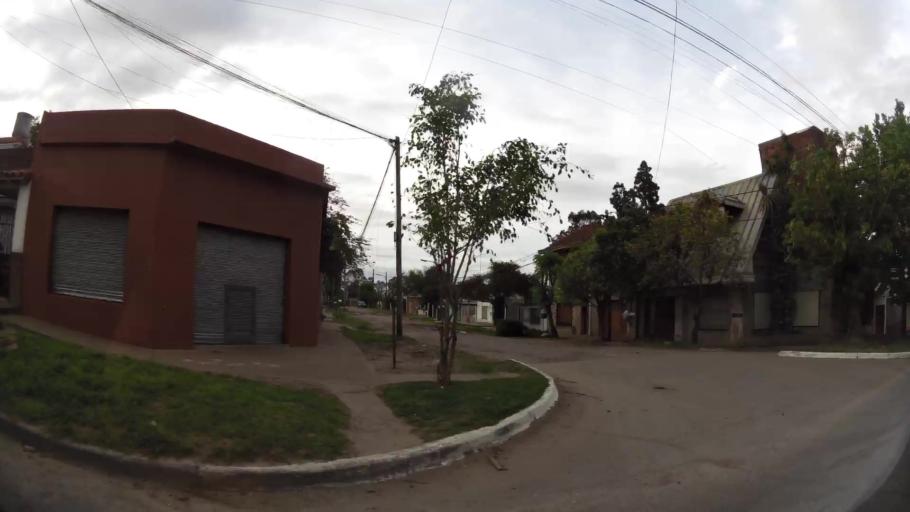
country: AR
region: Buenos Aires
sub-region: Partido de Quilmes
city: Quilmes
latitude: -34.7255
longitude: -58.2368
